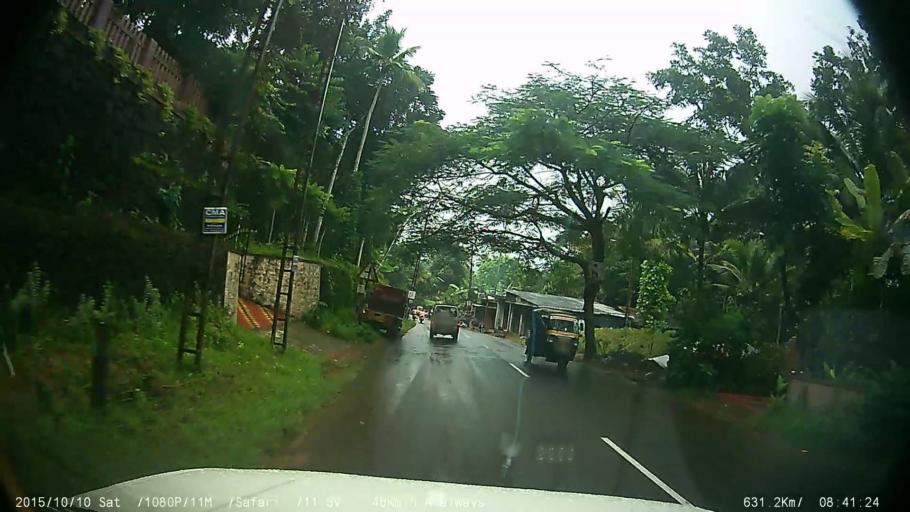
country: IN
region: Kerala
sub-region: Kottayam
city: Palackattumala
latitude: 9.7551
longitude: 76.5439
